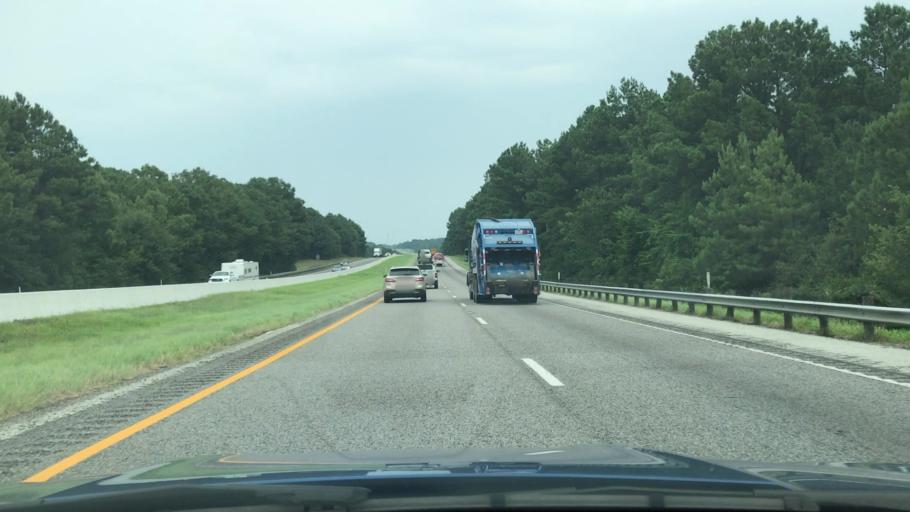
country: US
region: Texas
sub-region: Smith County
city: Lindale
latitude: 32.4610
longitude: -95.3210
